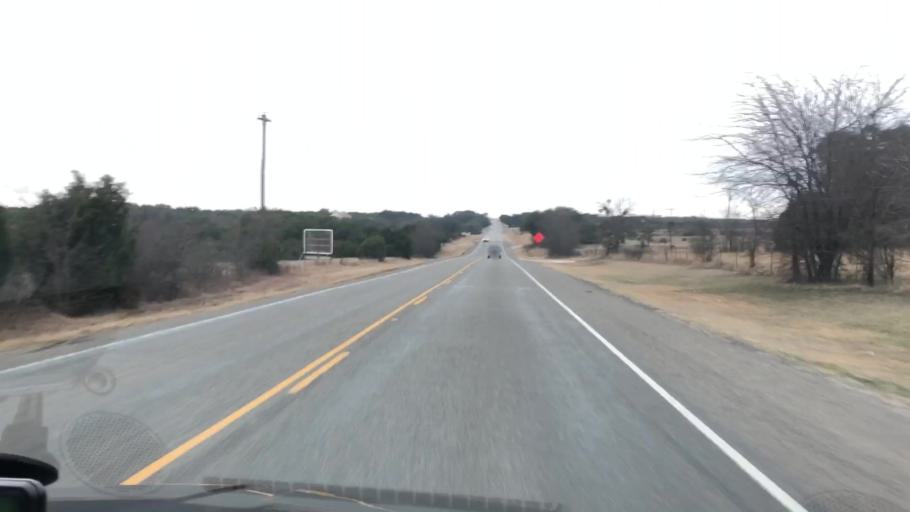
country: US
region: Texas
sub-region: Hamilton County
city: Hico
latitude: 31.9948
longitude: -98.0455
